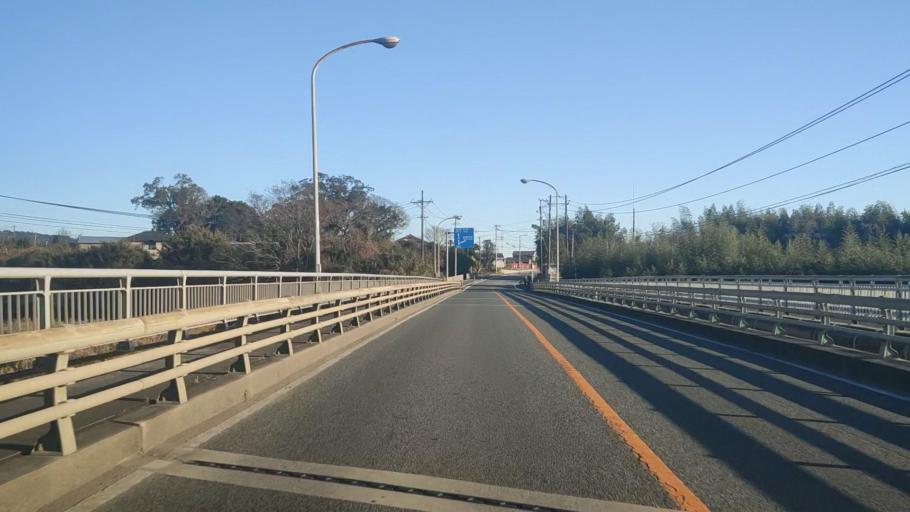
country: JP
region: Miyazaki
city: Takanabe
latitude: 32.2407
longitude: 131.5488
